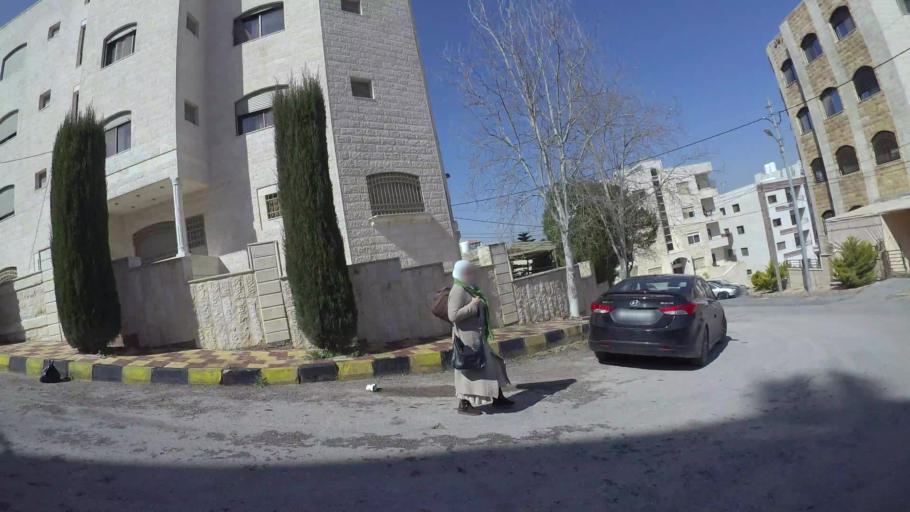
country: JO
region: Amman
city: Al Bunayyat ash Shamaliyah
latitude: 31.8938
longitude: 35.8995
